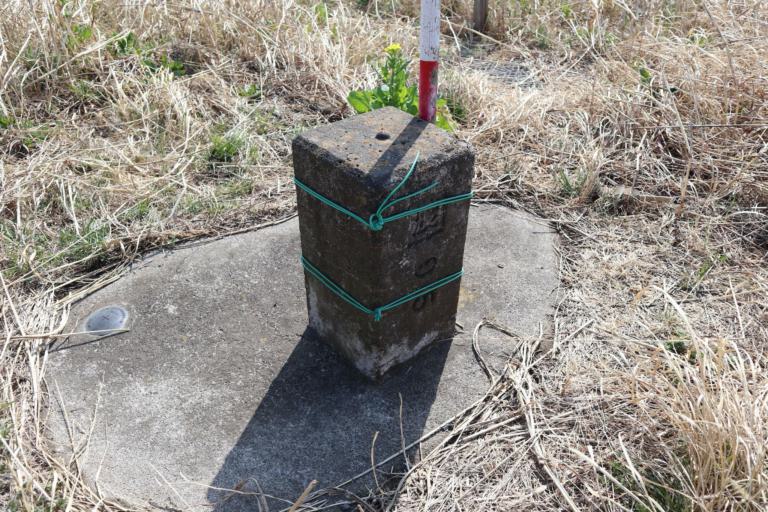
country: JP
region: Ibaraki
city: Koga
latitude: 36.1654
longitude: 139.6916
